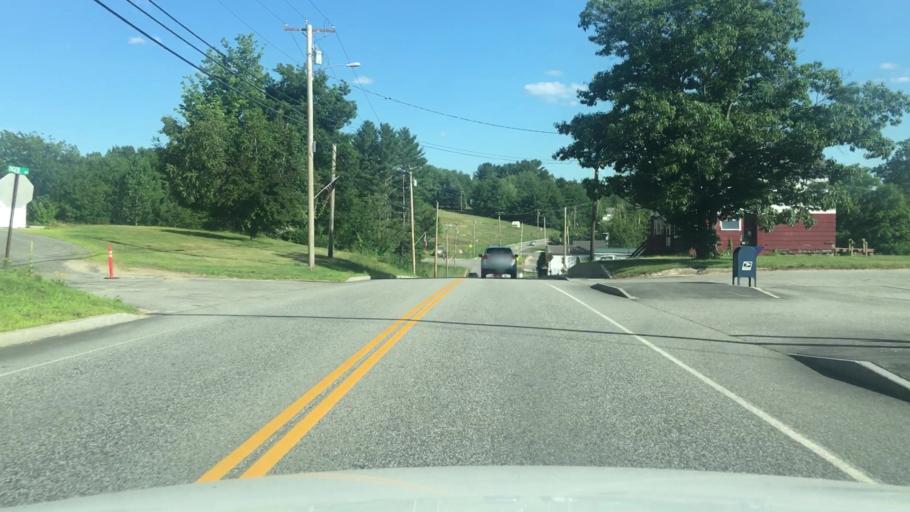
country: US
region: Maine
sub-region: Franklin County
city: Jay
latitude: 44.4958
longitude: -70.2045
